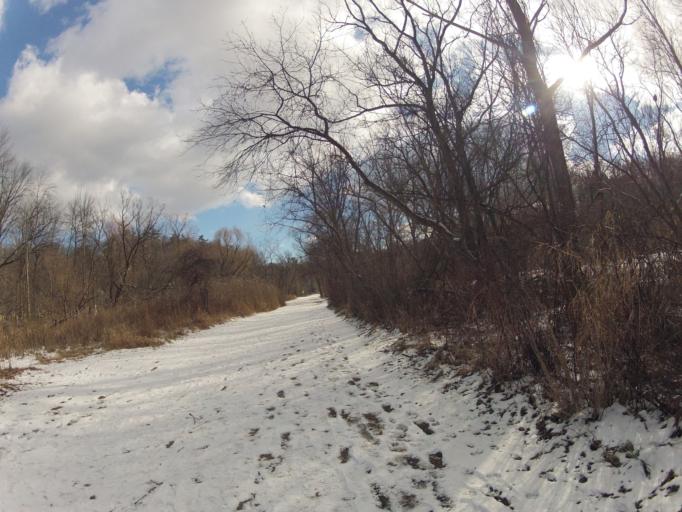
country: CA
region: Ontario
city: Mississauga
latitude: 43.5594
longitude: -79.6700
